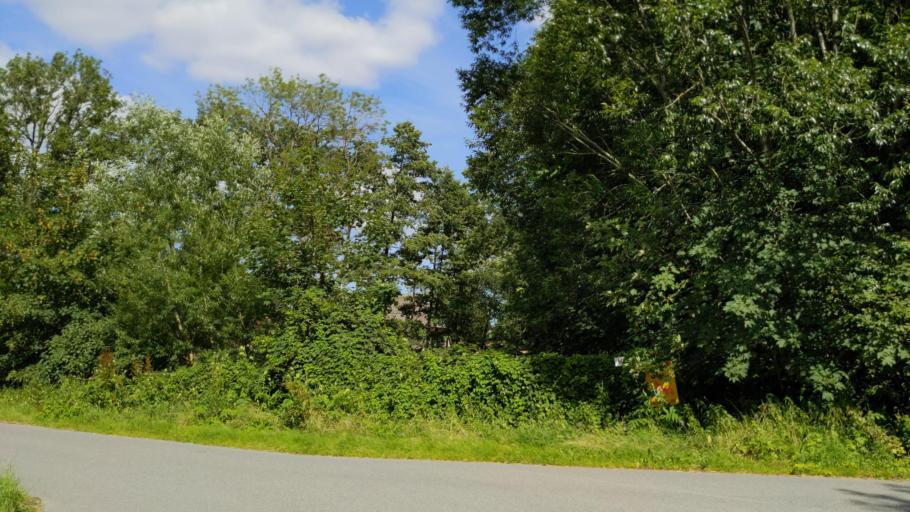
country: DE
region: Schleswig-Holstein
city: Altenkrempe
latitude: 54.1566
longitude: 10.8300
